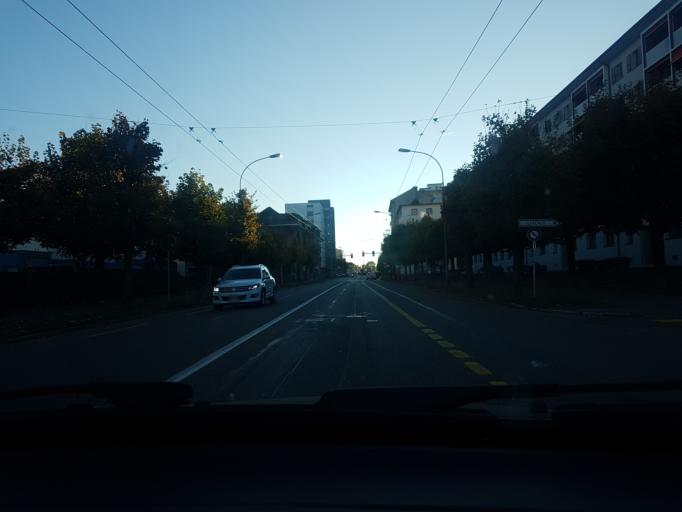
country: CH
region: Neuchatel
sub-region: La Chaux-de-Fonds District
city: La Chaux-de-Fonds
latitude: 47.0933
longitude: 6.8139
